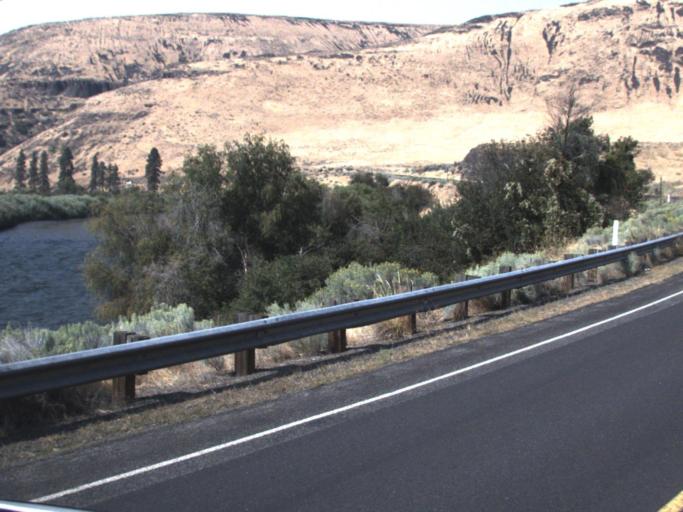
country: US
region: Washington
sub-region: Kittitas County
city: Kittitas
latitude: 46.8491
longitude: -120.4611
